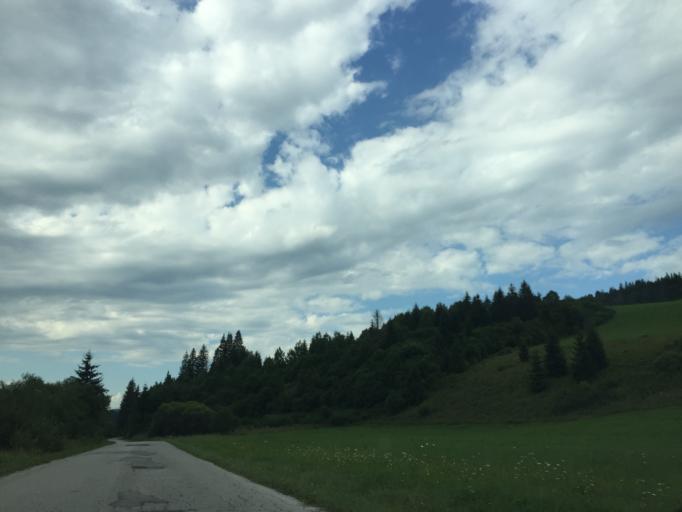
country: SK
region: Zilinsky
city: Namestovo
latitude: 49.3974
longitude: 19.3351
